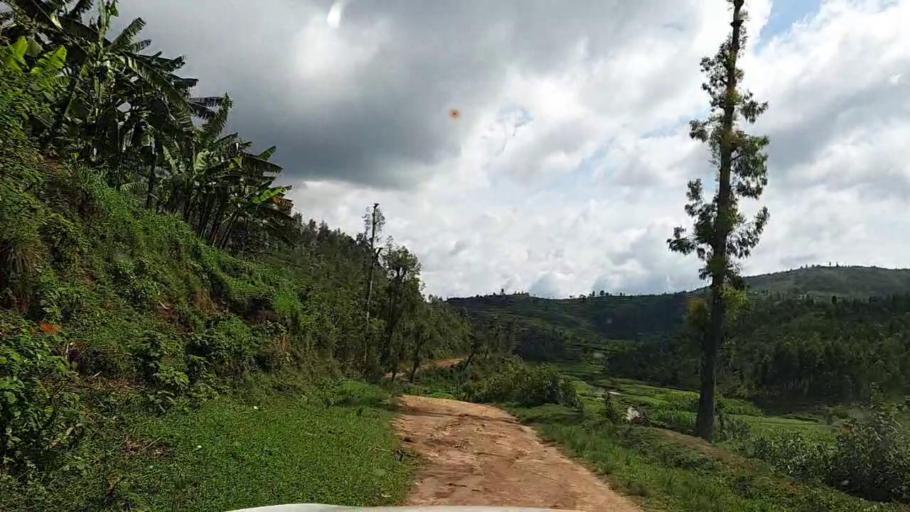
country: RW
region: Southern Province
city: Gikongoro
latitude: -2.3841
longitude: 29.5480
